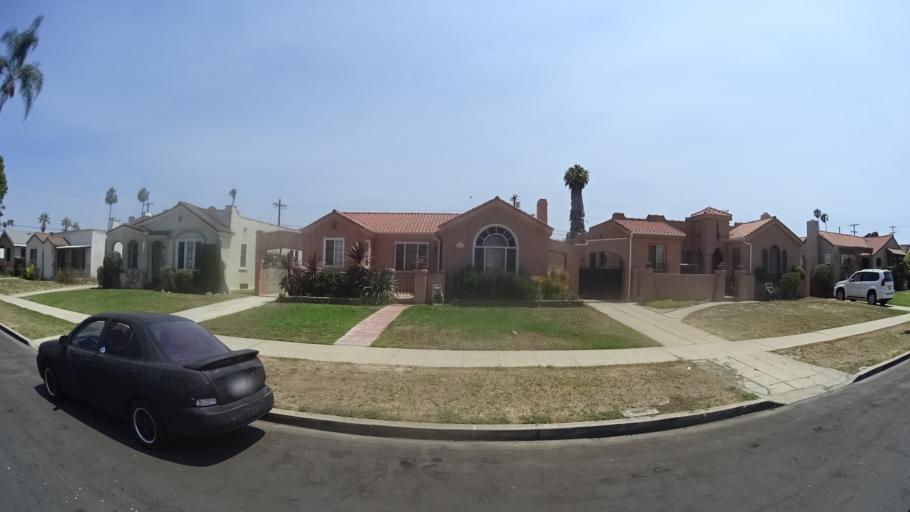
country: US
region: California
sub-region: Los Angeles County
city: Westmont
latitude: 33.9655
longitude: -118.3101
